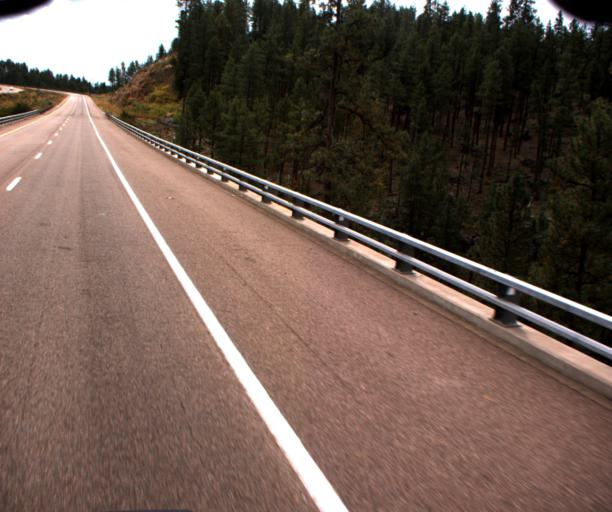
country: US
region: Arizona
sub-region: Gila County
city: Star Valley
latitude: 34.3123
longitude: -111.0275
